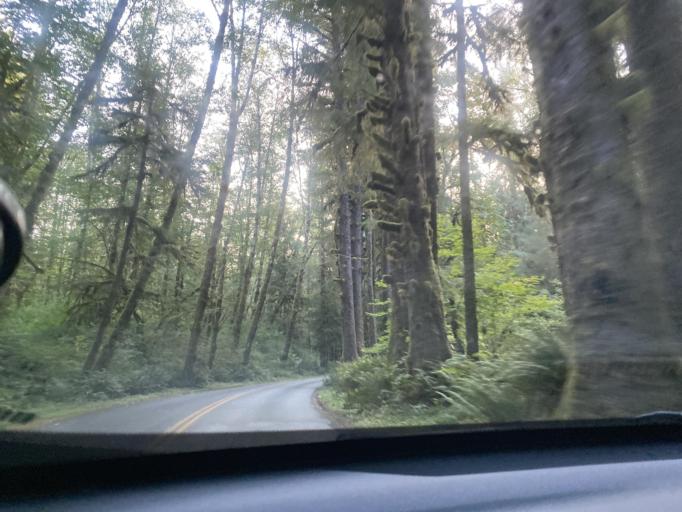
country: US
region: Washington
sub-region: Clallam County
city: Forks
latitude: 47.8154
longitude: -124.0632
